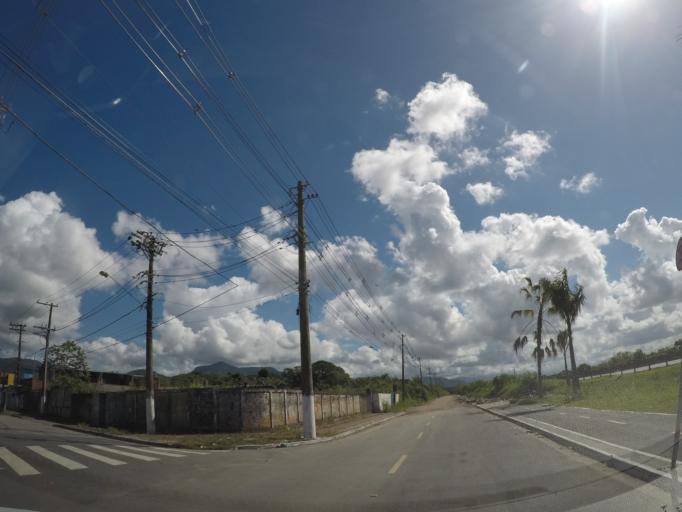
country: BR
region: Sao Paulo
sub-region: Praia Grande
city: Praia Grande
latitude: -24.0228
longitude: -46.5055
